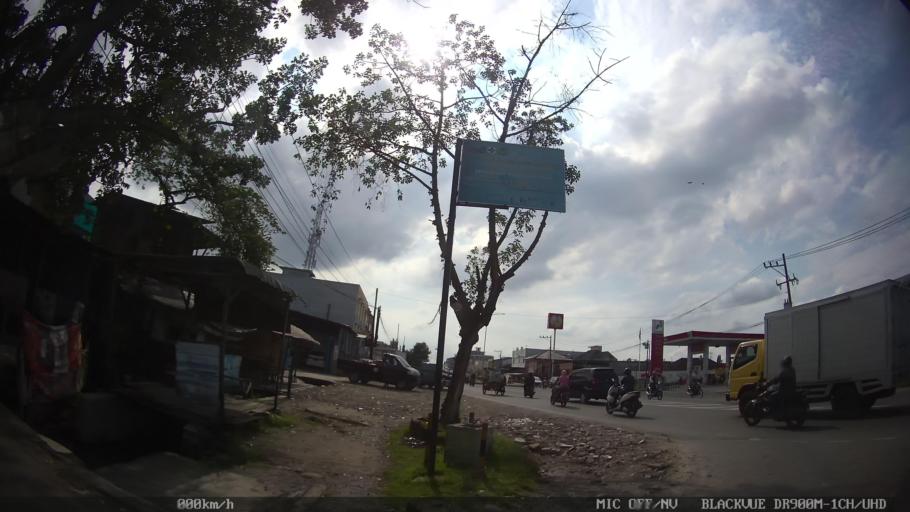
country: ID
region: North Sumatra
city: Medan
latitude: 3.6153
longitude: 98.6451
